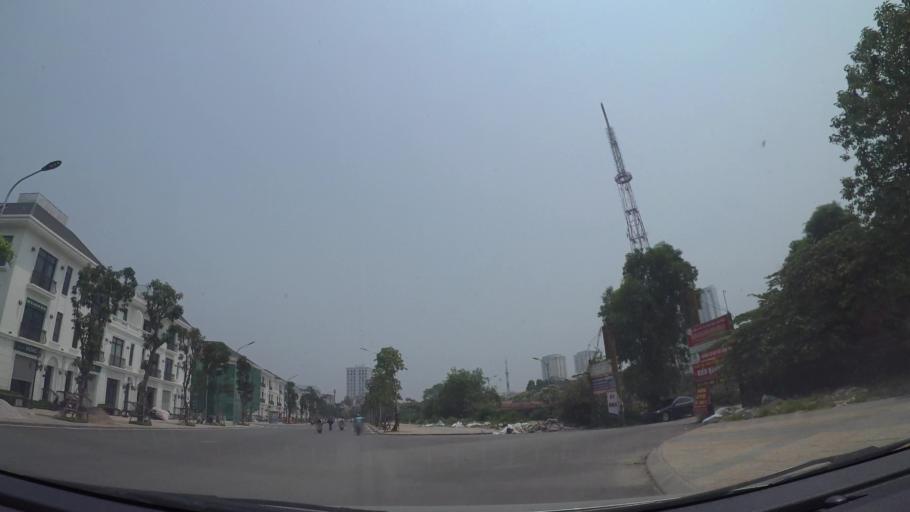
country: VN
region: Ha Noi
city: Thanh Xuan
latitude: 20.9992
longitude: 105.7851
